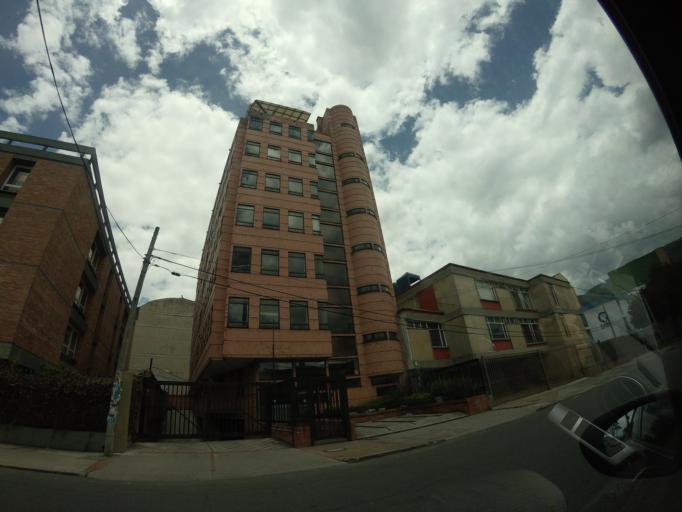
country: CO
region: Bogota D.C.
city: Barrio San Luis
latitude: 4.6692
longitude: -74.0594
